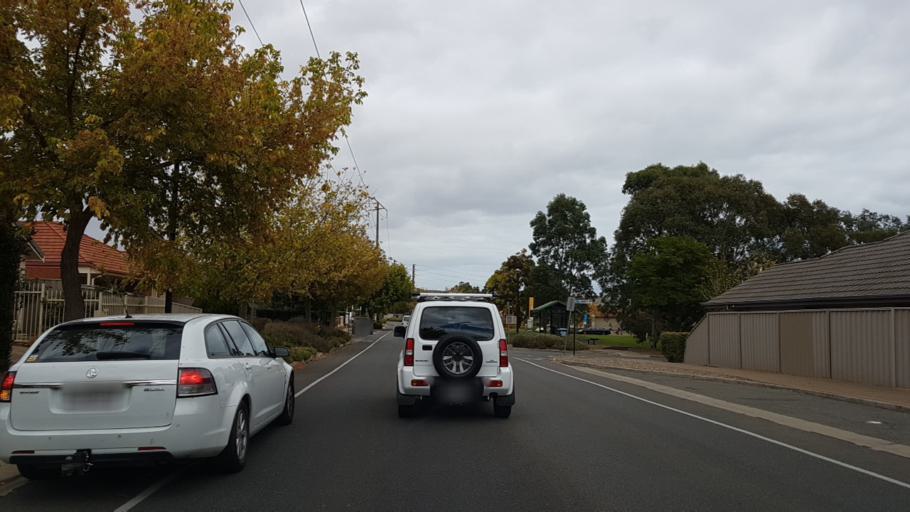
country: AU
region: South Australia
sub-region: Marion
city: Marion
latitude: -35.0148
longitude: 138.5650
